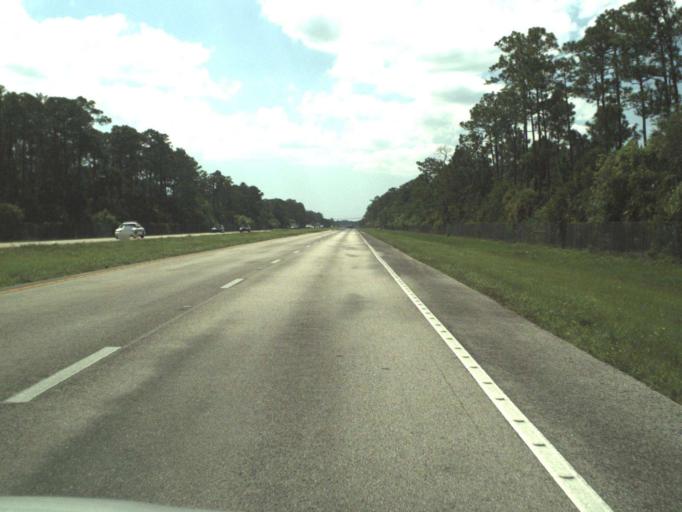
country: US
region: Florida
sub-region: Brevard County
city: Cocoa West
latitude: 28.3725
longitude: -80.8998
